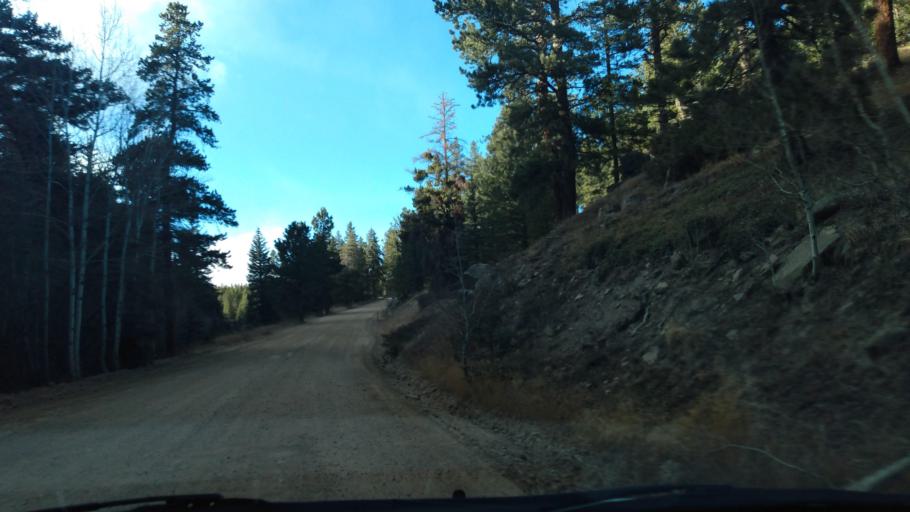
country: US
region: Colorado
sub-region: Boulder County
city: Nederland
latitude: 39.9467
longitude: -105.4485
